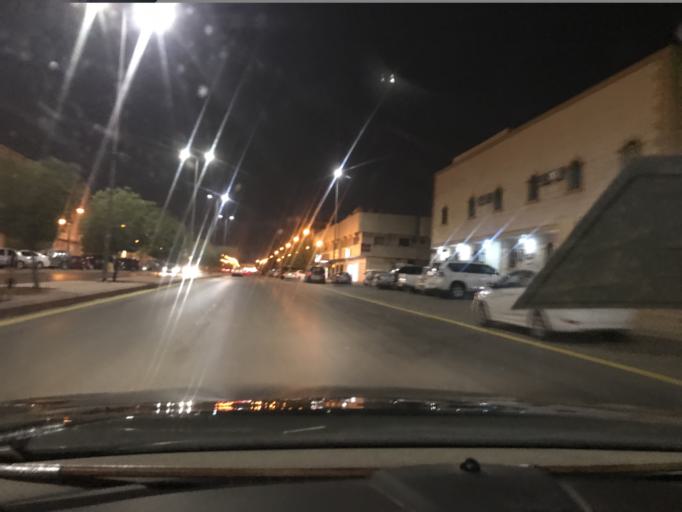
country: SA
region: Ar Riyad
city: Riyadh
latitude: 24.7405
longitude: 46.7706
